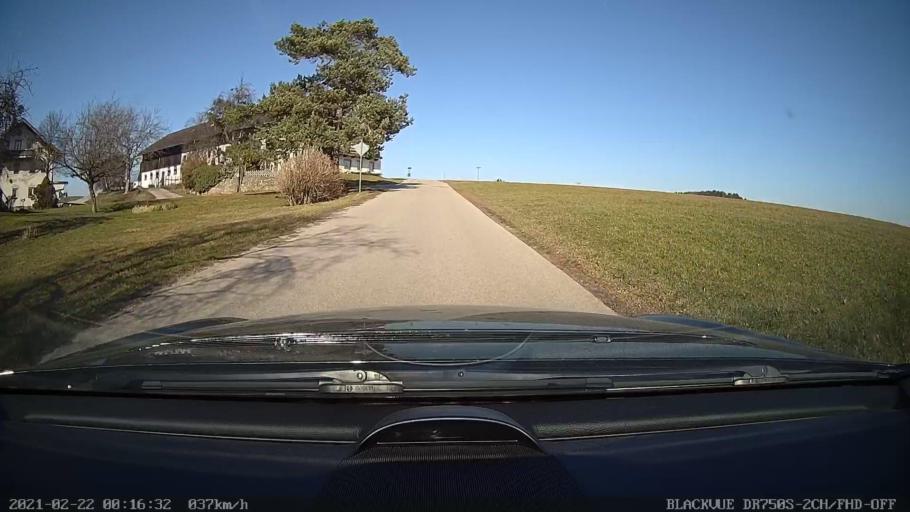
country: DE
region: Bavaria
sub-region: Upper Bavaria
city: Griesstatt
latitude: 47.9766
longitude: 12.1975
